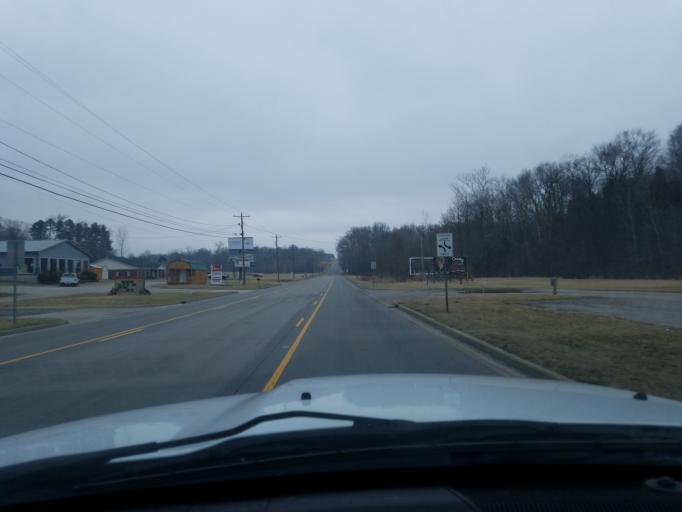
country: US
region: Indiana
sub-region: Perry County
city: Tell City
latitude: 37.9651
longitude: -86.7455
